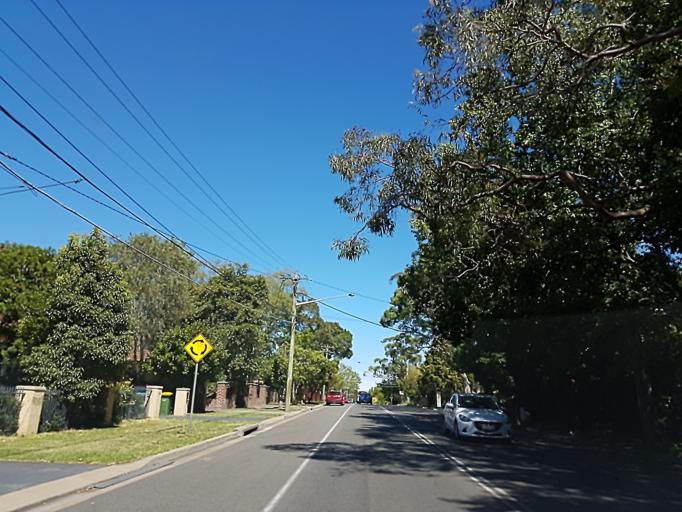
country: AU
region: New South Wales
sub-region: Ku-ring-gai
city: North Wahroonga
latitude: -33.7093
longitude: 151.1239
